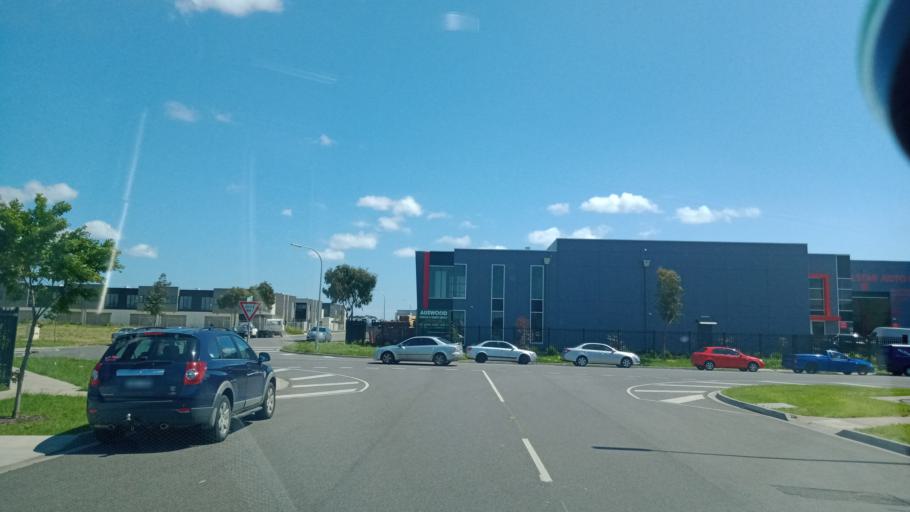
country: AU
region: Victoria
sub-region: Casey
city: Cranbourne West
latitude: -38.0931
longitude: 145.2536
